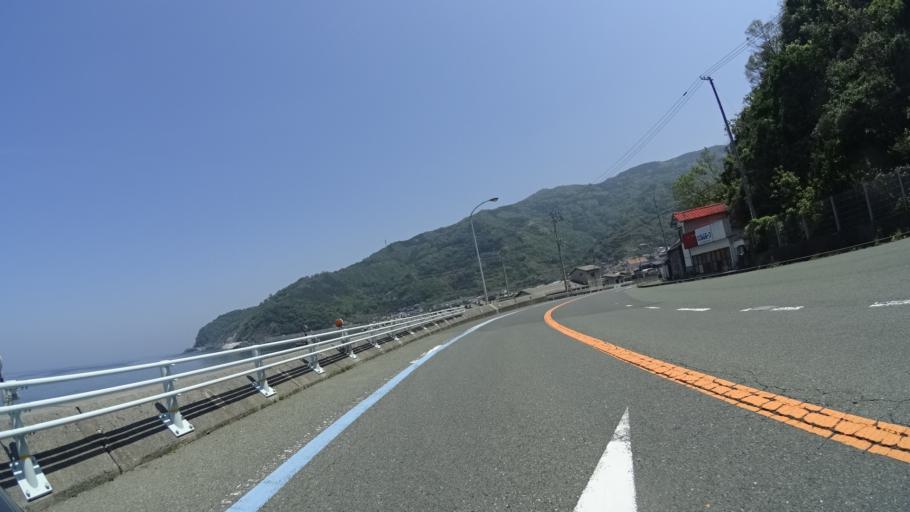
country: JP
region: Ehime
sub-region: Nishiuwa-gun
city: Ikata-cho
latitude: 33.5579
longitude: 132.4303
